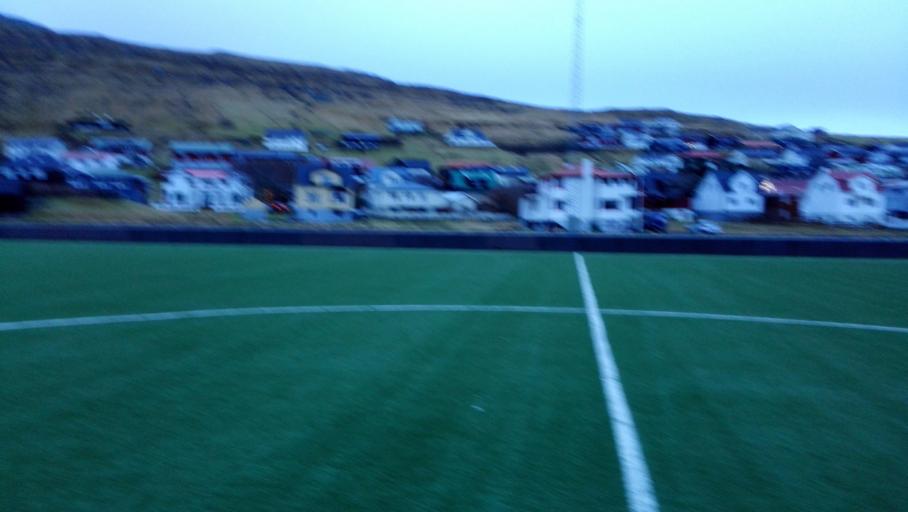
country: FO
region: Vagar
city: Midvagur
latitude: 62.0553
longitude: -7.1516
